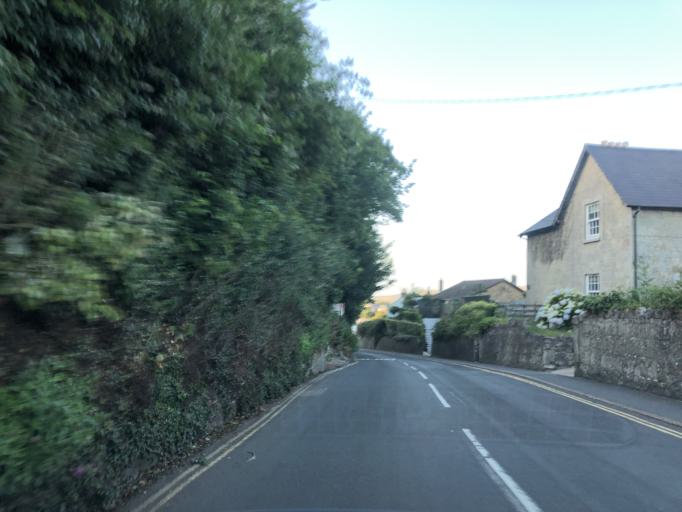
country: GB
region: England
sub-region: Isle of Wight
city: Niton
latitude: 50.5859
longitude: -1.2856
